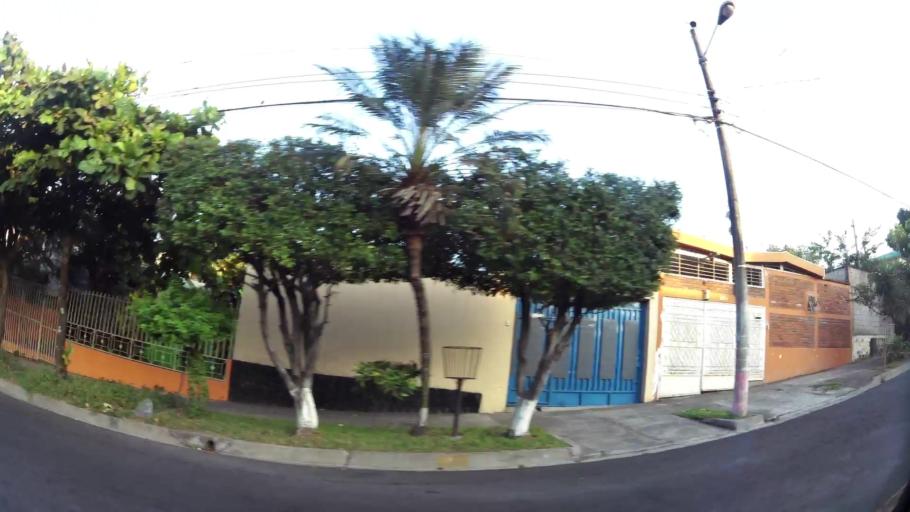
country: SV
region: San Salvador
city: San Salvador
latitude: 13.6841
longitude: -89.2103
